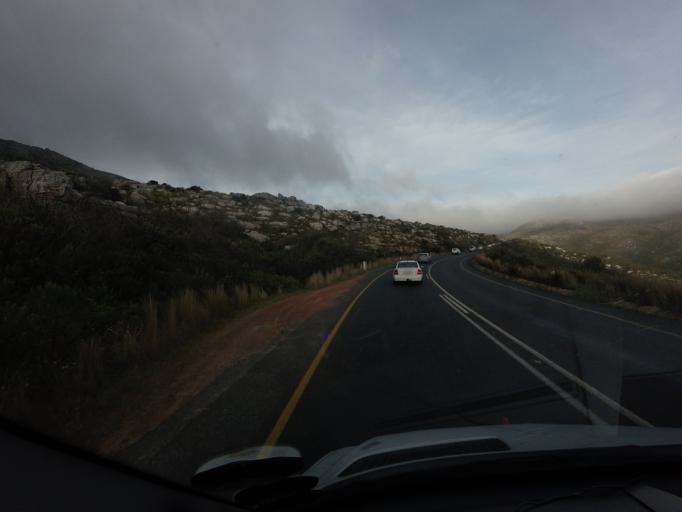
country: ZA
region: Western Cape
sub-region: City of Cape Town
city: Bergvliet
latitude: -34.1015
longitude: 18.4136
